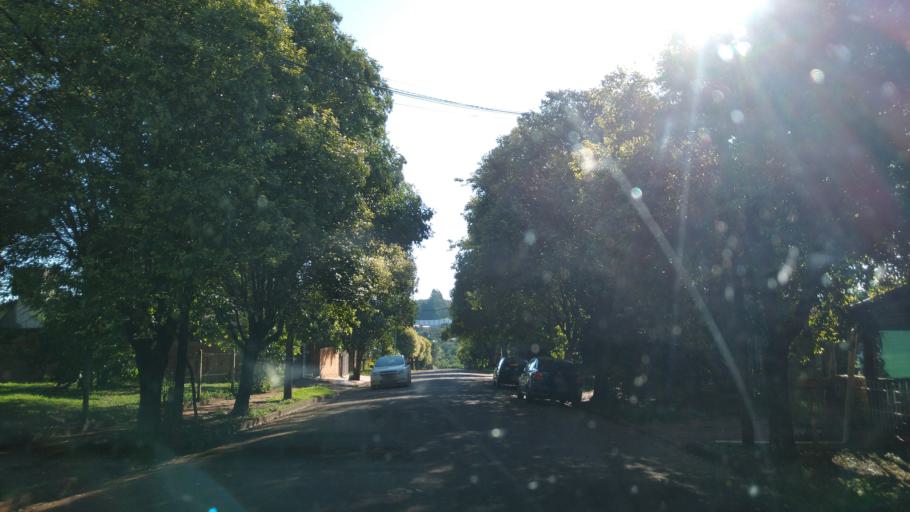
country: AR
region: Misiones
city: Garuhape
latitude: -26.8216
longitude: -54.9593
